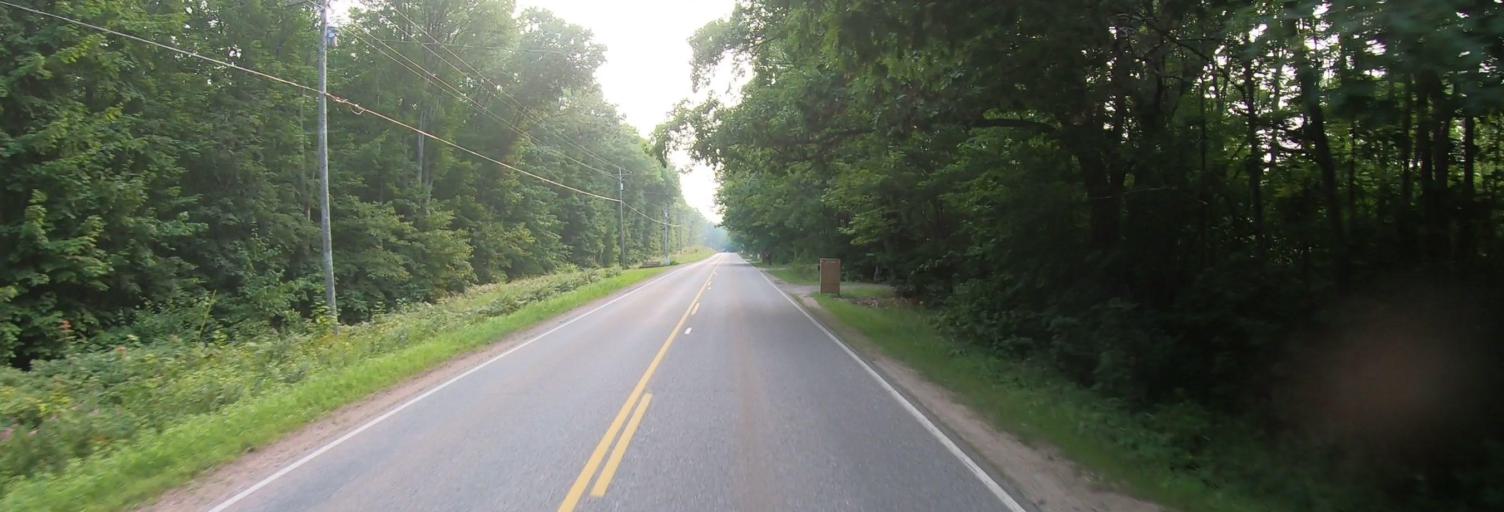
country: US
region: Michigan
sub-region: Chippewa County
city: Sault Ste. Marie
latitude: 46.4832
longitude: -84.6404
